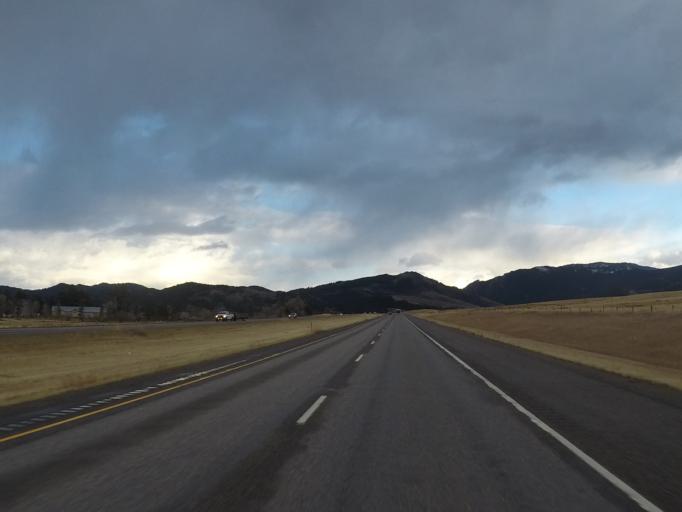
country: US
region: Montana
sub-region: Gallatin County
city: Bozeman
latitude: 45.6655
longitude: -110.9780
